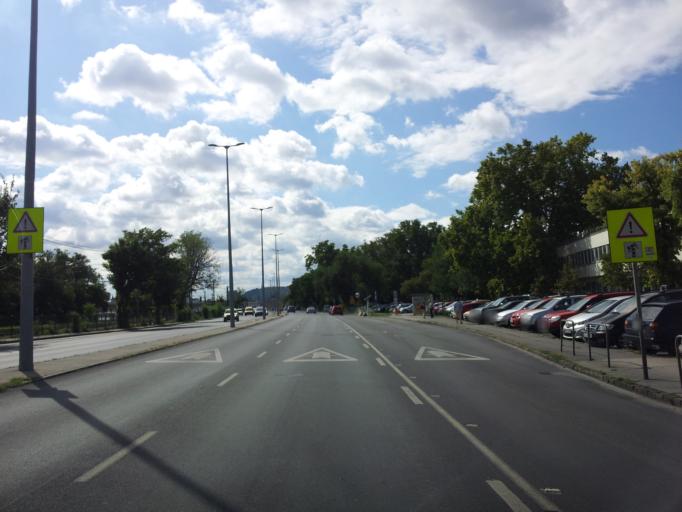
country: HU
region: Budapest
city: Budapest II. keruelet
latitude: 47.5203
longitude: 19.0381
